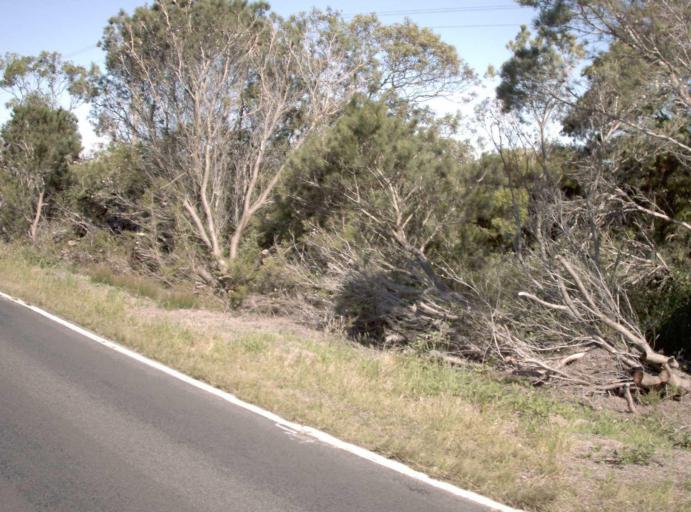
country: AU
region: Victoria
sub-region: Latrobe
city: Morwell
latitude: -38.6356
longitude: 146.5317
